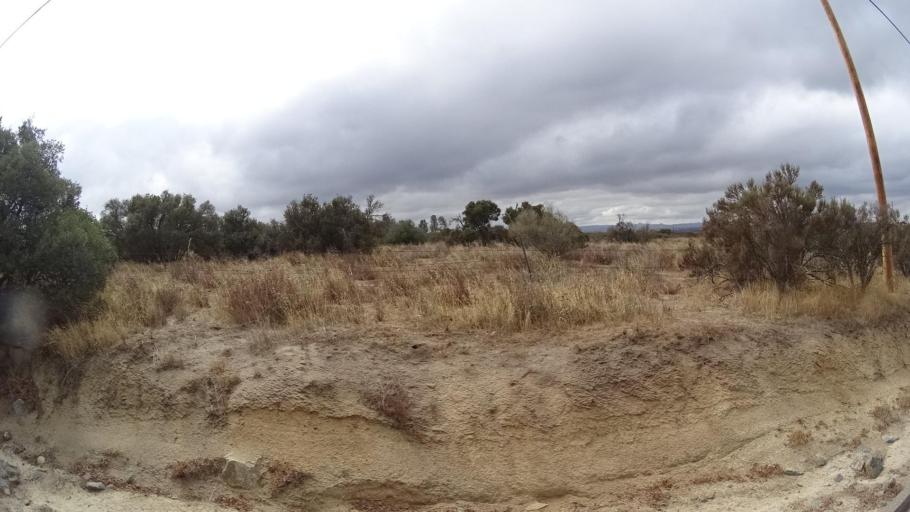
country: US
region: California
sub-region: San Diego County
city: Campo
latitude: 32.6095
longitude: -116.3322
